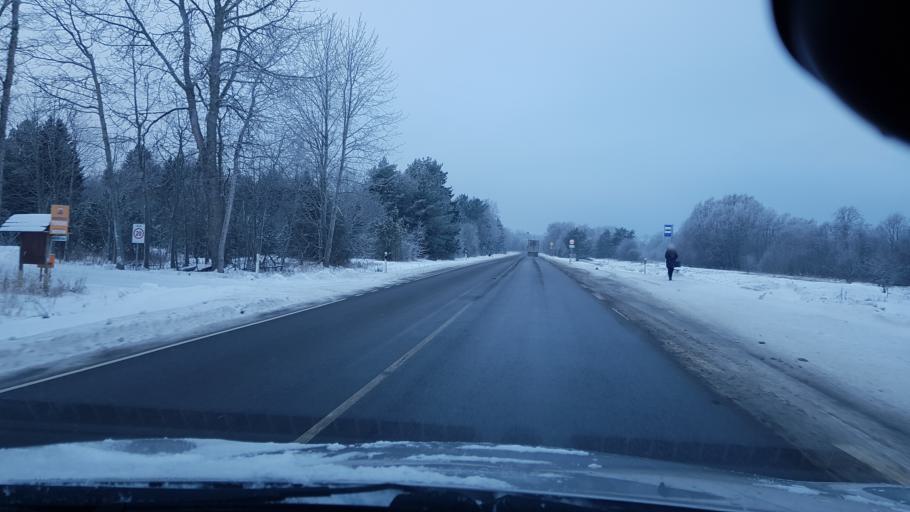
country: EE
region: Harju
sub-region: Paldiski linn
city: Paldiski
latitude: 59.3428
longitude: 24.1948
